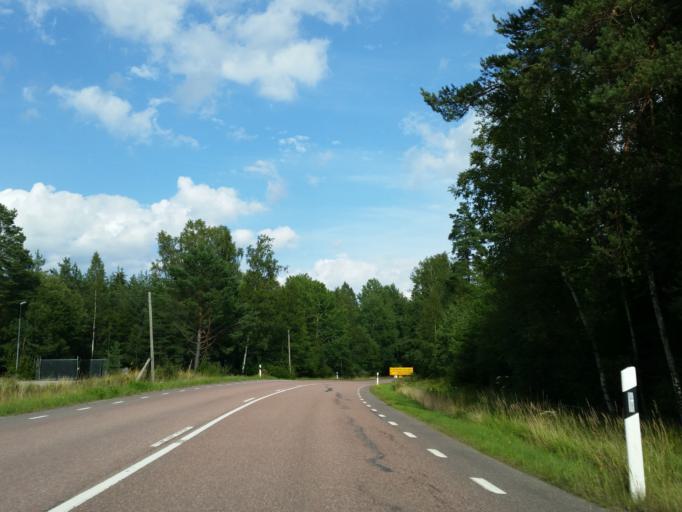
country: SE
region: Soedermanland
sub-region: Strangnas Kommun
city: Mariefred
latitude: 59.2219
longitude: 17.2592
